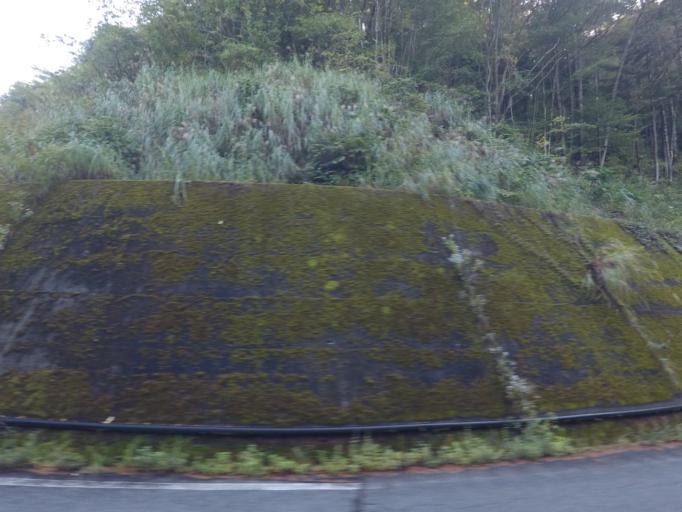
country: JP
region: Nagano
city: Tatsuno
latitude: 35.9710
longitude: 137.7745
